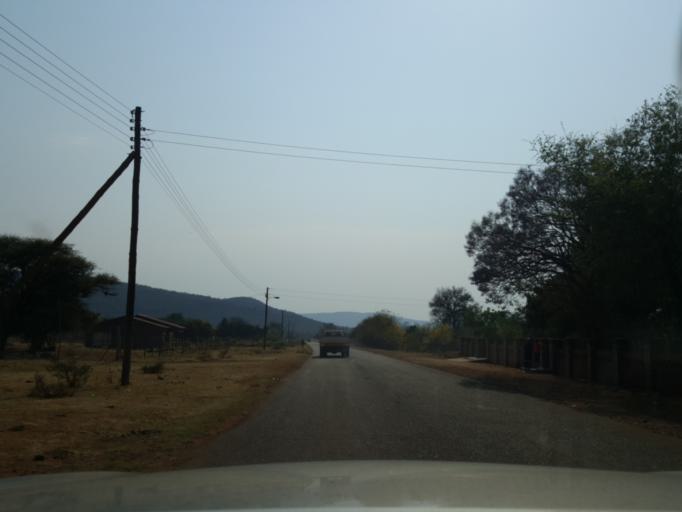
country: BW
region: South East
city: Lobatse
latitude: -25.3099
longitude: 25.8101
